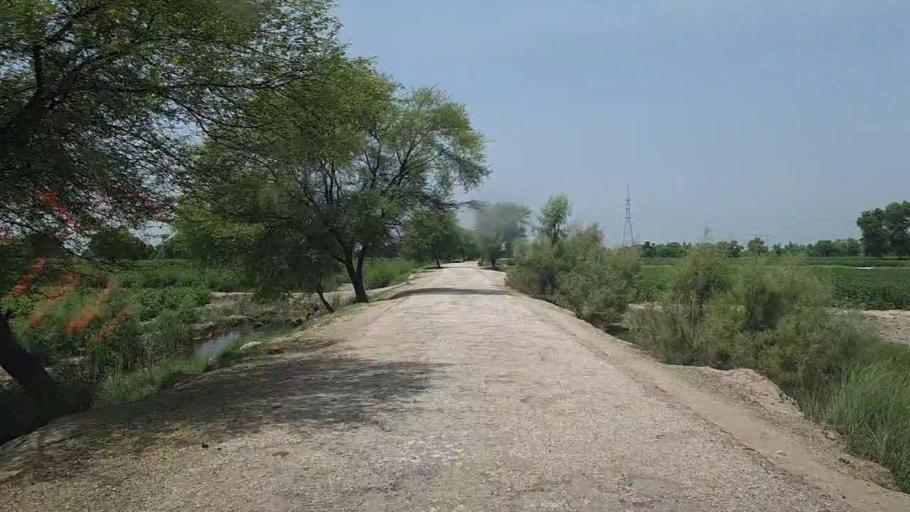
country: PK
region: Sindh
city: Pano Aqil
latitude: 27.8236
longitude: 69.2180
